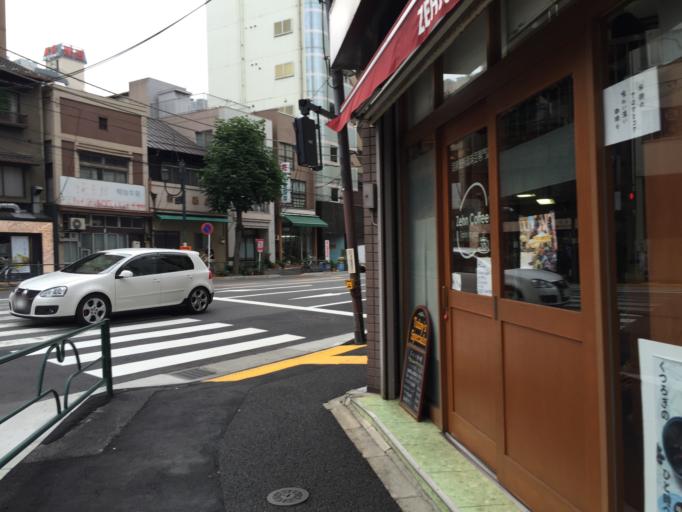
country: JP
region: Tokyo
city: Tokyo
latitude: 35.7065
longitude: 139.7701
